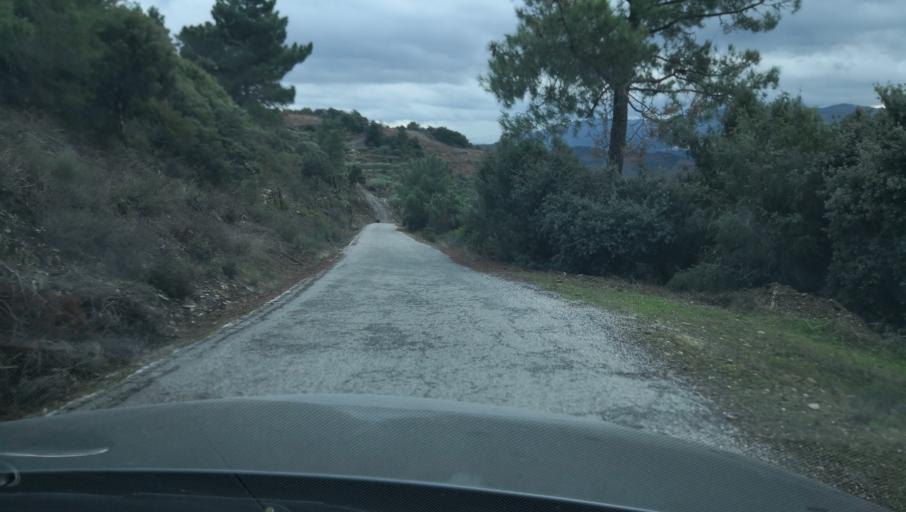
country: PT
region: Vila Real
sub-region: Sabrosa
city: Vilela
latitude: 41.1845
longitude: -7.5730
